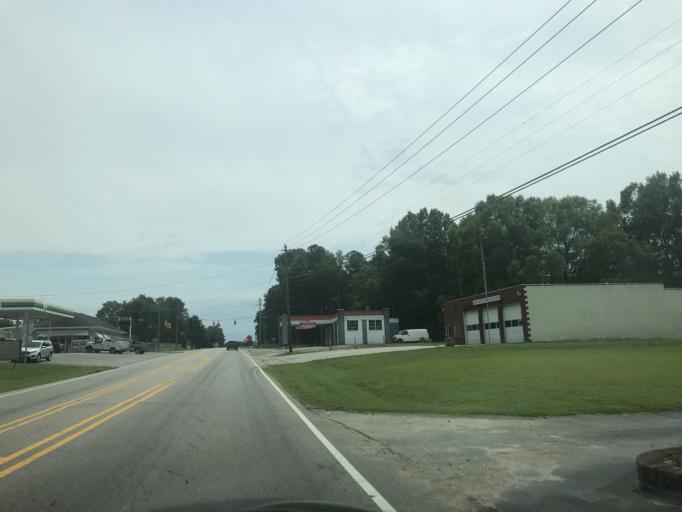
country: US
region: North Carolina
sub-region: Vance County
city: South Henderson
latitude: 36.2781
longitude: -78.4060
